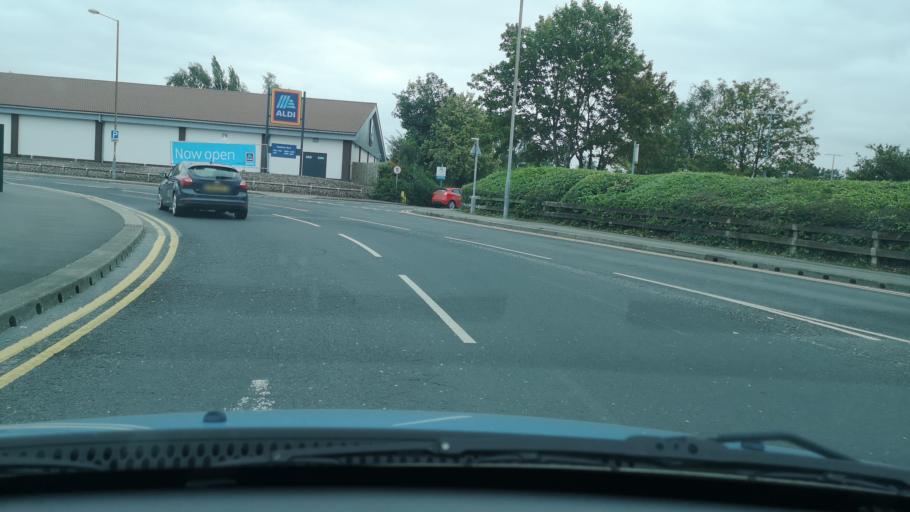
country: GB
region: England
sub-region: City and Borough of Wakefield
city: Castleford
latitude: 53.7243
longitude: -1.3586
